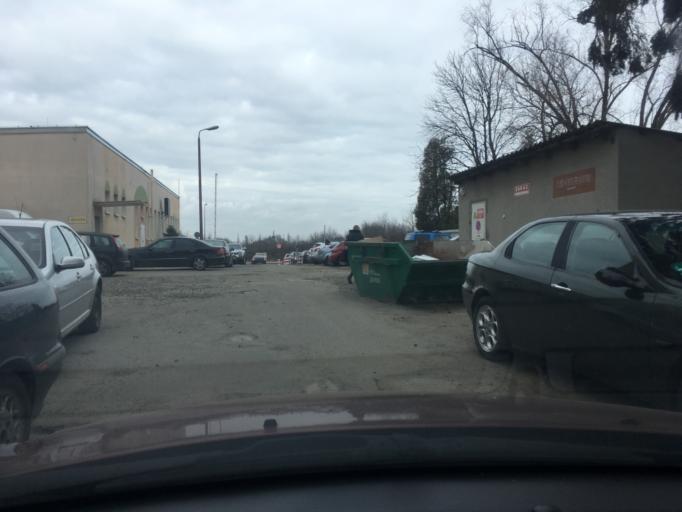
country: PL
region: Lower Silesian Voivodeship
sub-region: Powiat zgorzelecki
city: Zgorzelec
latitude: 51.1576
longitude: 15.0118
